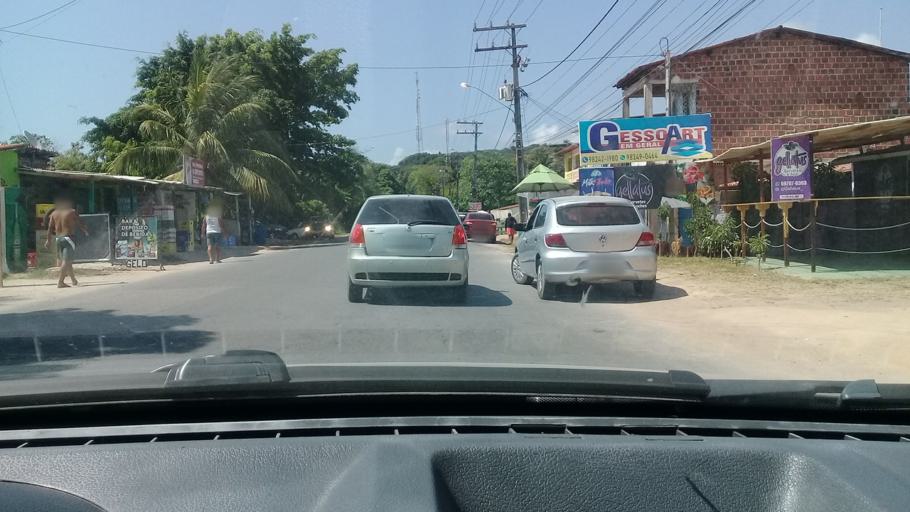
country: BR
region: Pernambuco
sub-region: Itamaraca
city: Itamaraca
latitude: -7.7715
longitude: -34.8362
